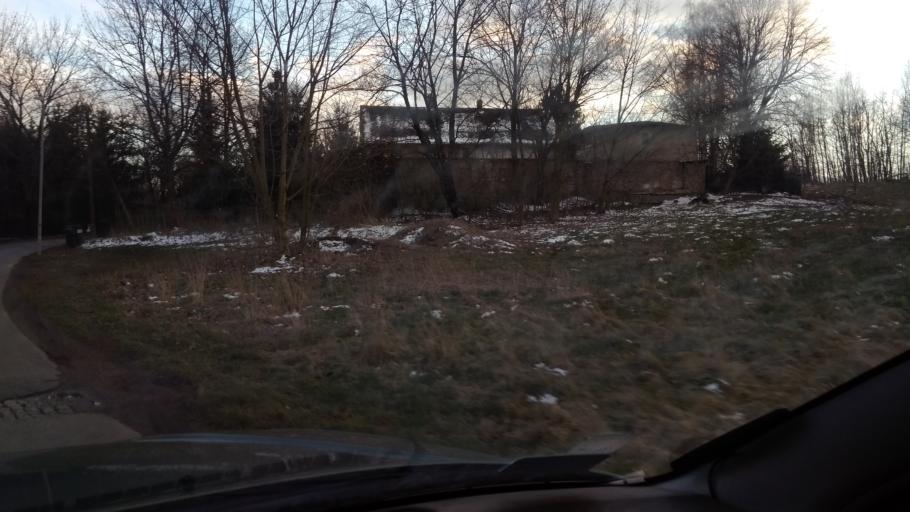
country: PL
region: Lower Silesian Voivodeship
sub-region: Powiat jeleniogorski
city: Sosnowka
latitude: 50.8436
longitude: 15.7389
